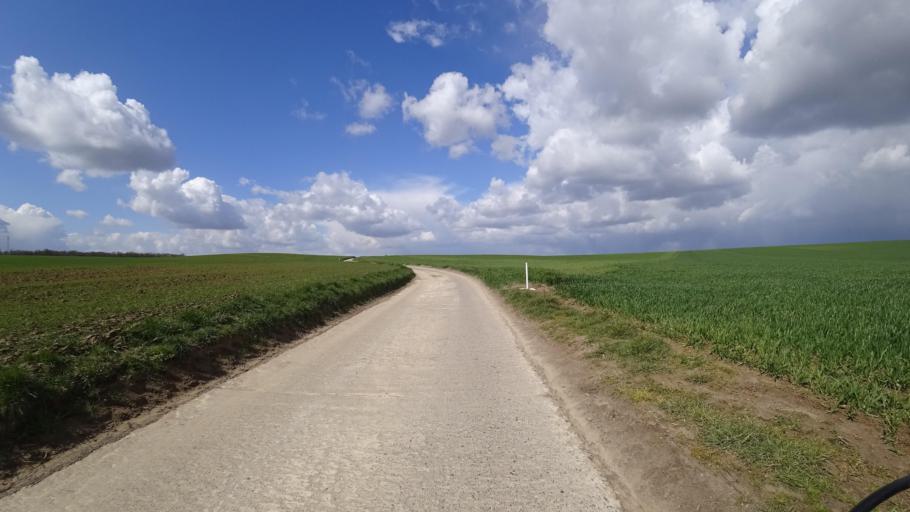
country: BE
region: Wallonia
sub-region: Province du Brabant Wallon
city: Chaumont-Gistoux
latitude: 50.6559
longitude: 4.7033
